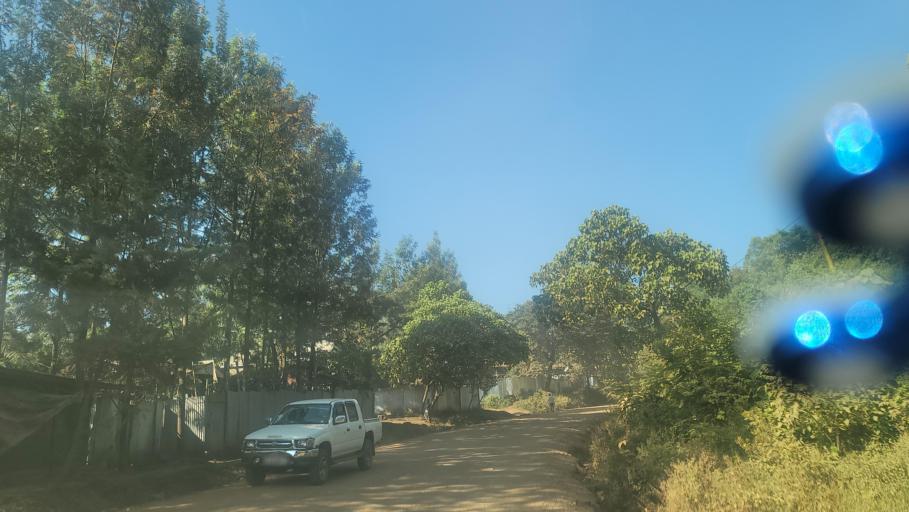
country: ET
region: Oromiya
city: Agaro
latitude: 7.8583
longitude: 36.5743
